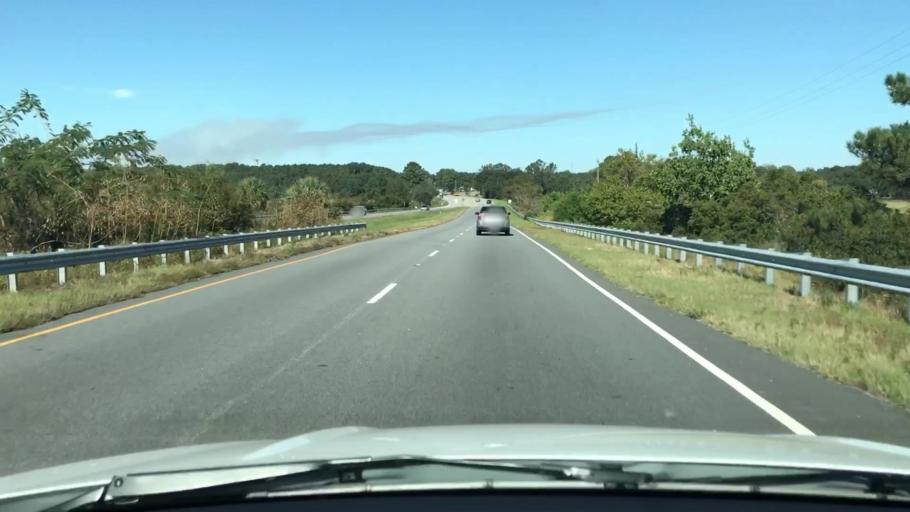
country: US
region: South Carolina
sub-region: Beaufort County
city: Laurel Bay
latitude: 32.5422
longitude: -80.7448
